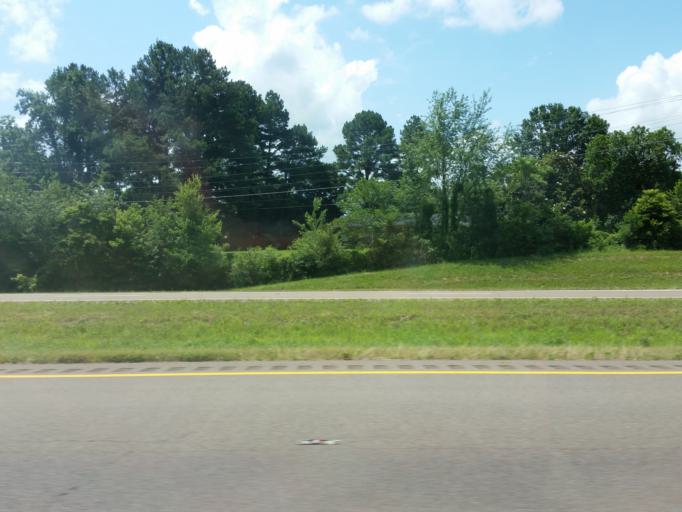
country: US
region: Tennessee
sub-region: Weakley County
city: Martin
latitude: 36.3698
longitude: -88.8560
